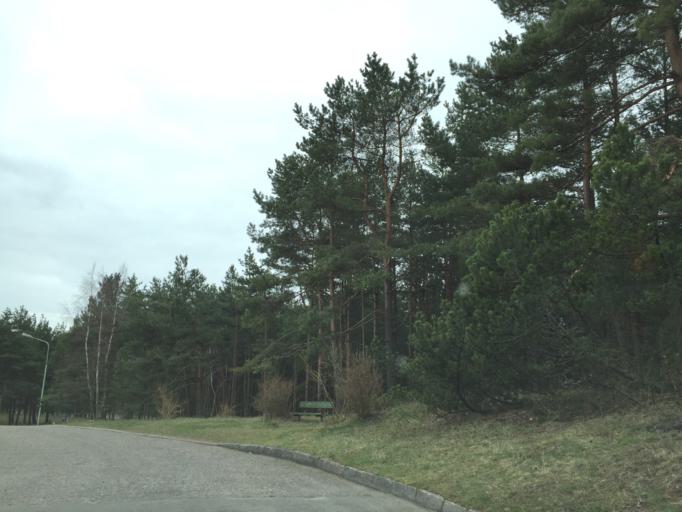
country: LT
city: Nida
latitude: 55.3036
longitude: 20.9971
